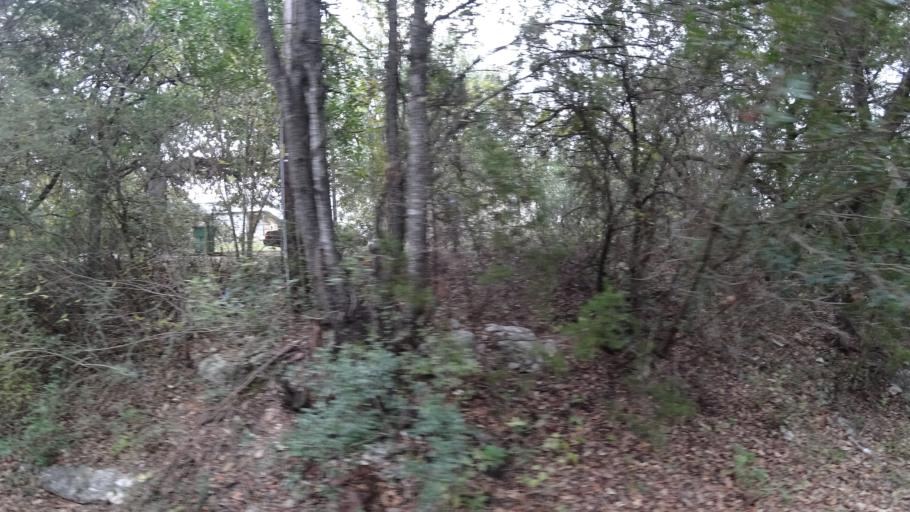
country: US
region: Texas
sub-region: Travis County
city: Bee Cave
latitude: 30.3309
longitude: -97.9268
